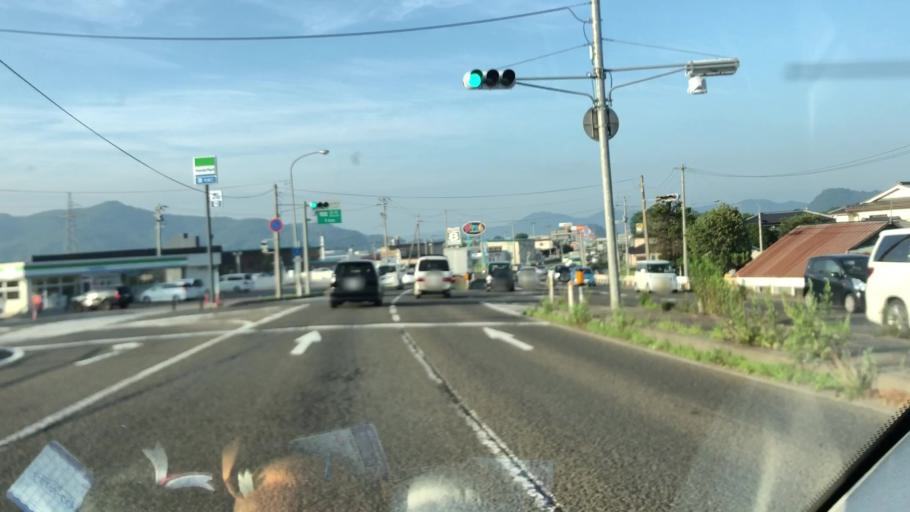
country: JP
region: Miyagi
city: Shiroishi
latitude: 38.0289
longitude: 140.6299
